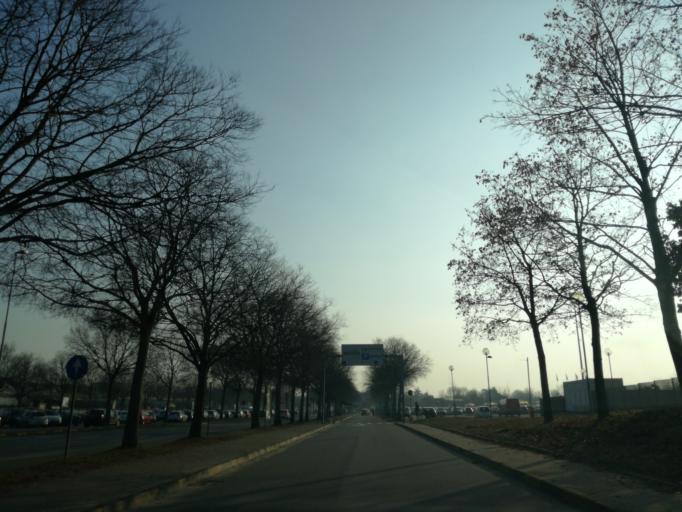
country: IT
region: Piedmont
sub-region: Provincia di Torino
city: Lesna
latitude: 45.0562
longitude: 7.6147
